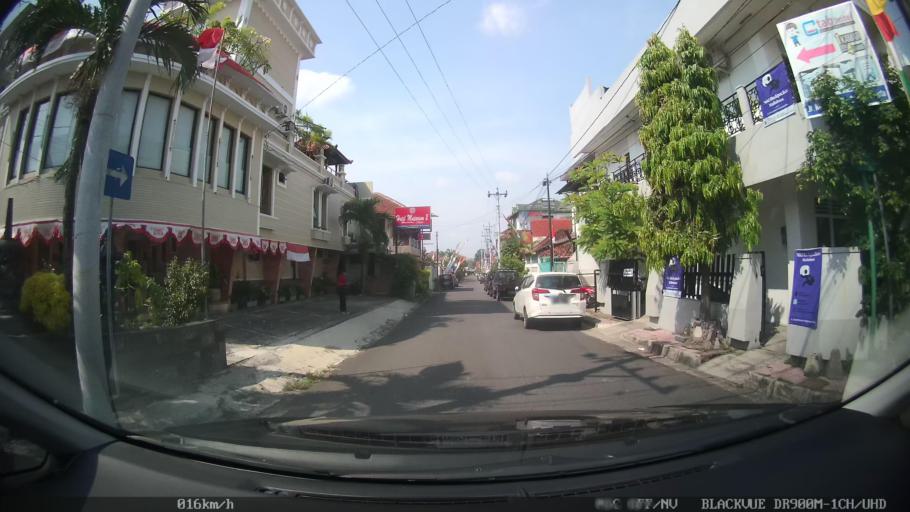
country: ID
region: Daerah Istimewa Yogyakarta
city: Yogyakarta
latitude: -7.7913
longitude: 110.3603
